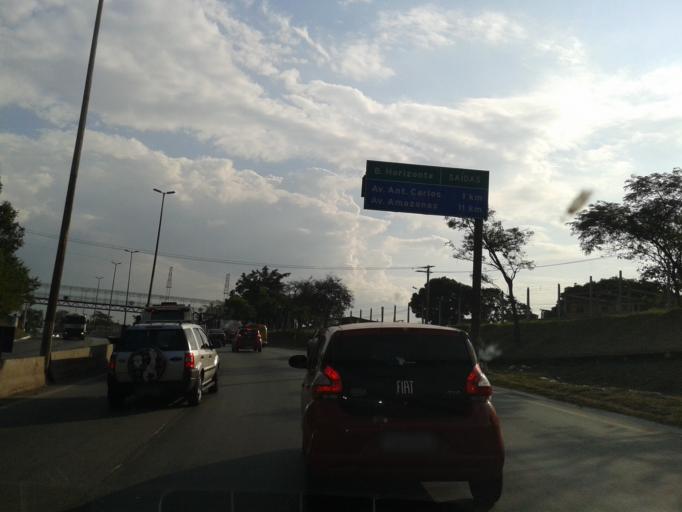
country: BR
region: Minas Gerais
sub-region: Belo Horizonte
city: Belo Horizonte
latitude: -19.8706
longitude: -43.9474
